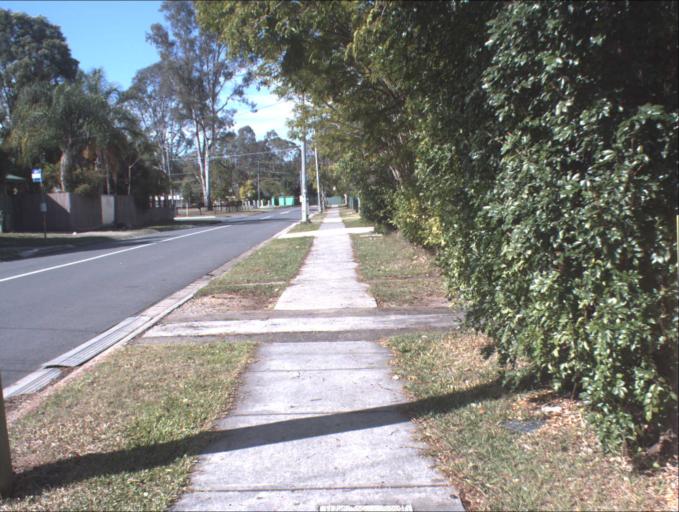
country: AU
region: Queensland
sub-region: Logan
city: Slacks Creek
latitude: -27.6459
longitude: 153.1334
